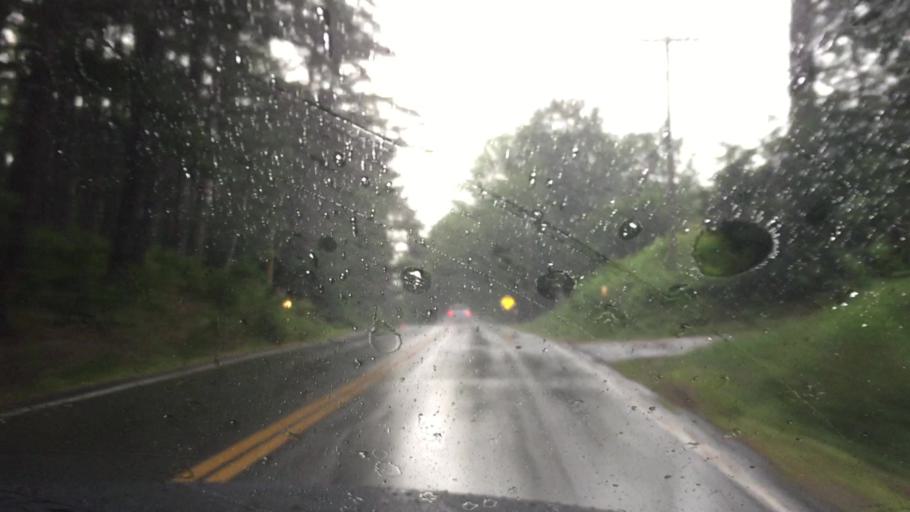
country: US
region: New Hampshire
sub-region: Grafton County
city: Holderness
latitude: 43.7189
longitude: -71.5376
